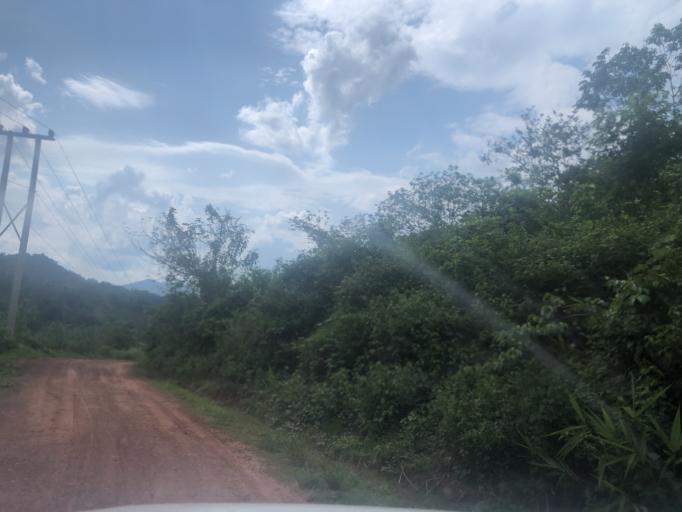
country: LA
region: Oudomxai
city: Muang La
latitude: 21.2409
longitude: 101.9465
